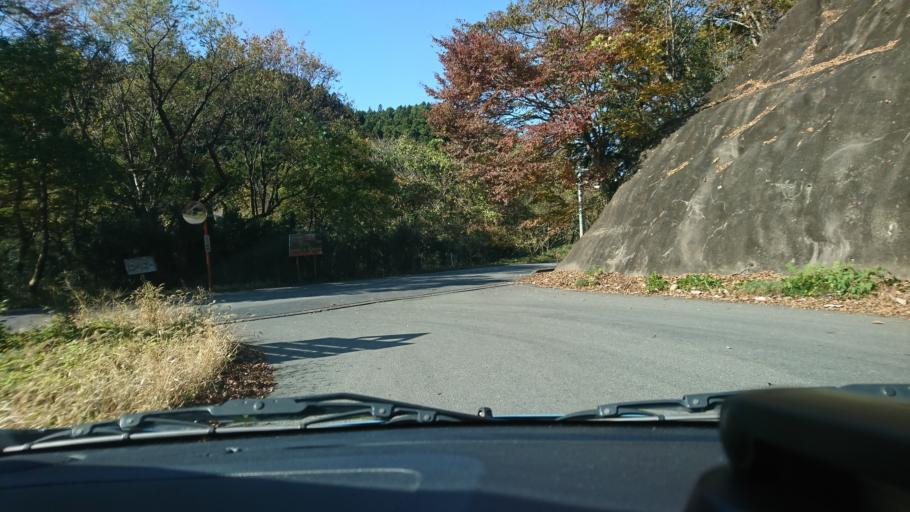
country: JP
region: Iwate
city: Ichinoseki
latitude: 38.7961
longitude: 141.2438
